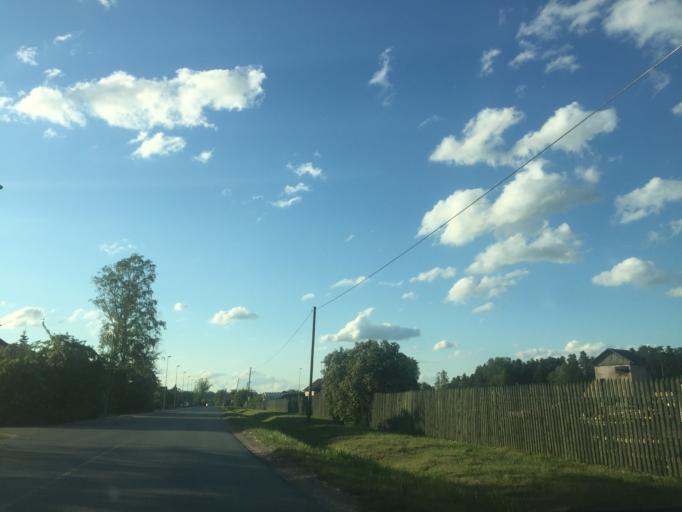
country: LV
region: Kandava
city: Kandava
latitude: 57.0259
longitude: 22.7925
